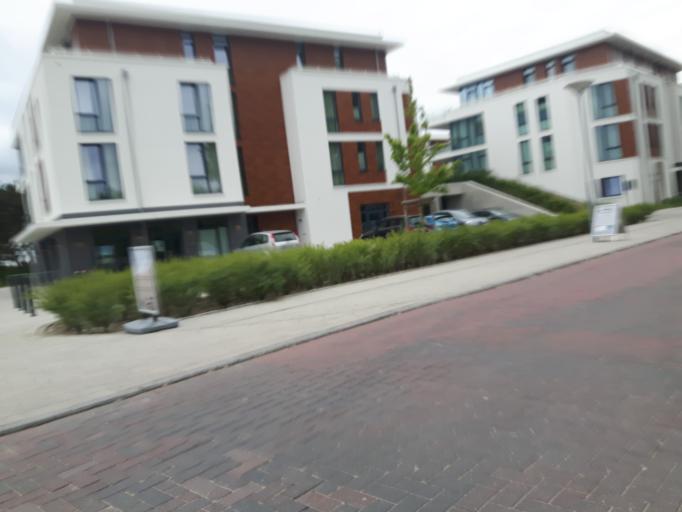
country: DE
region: Schleswig-Holstein
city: Schashagen
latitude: 54.0879
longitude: 10.8634
